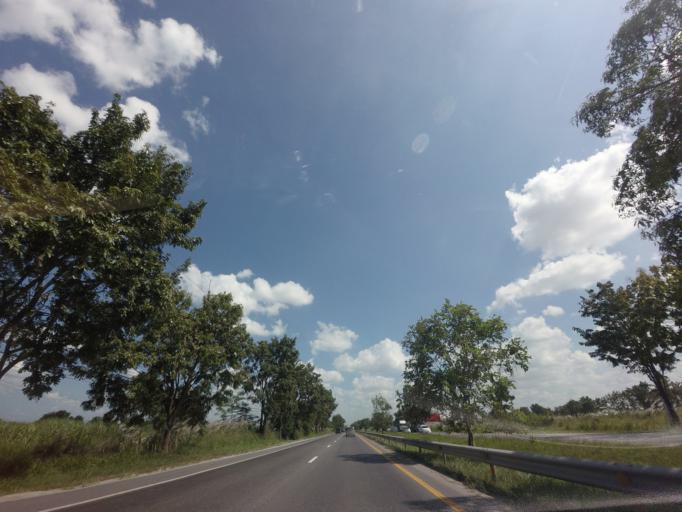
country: TH
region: Chon Buri
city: Ban Bueng
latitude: 13.2940
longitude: 101.1669
